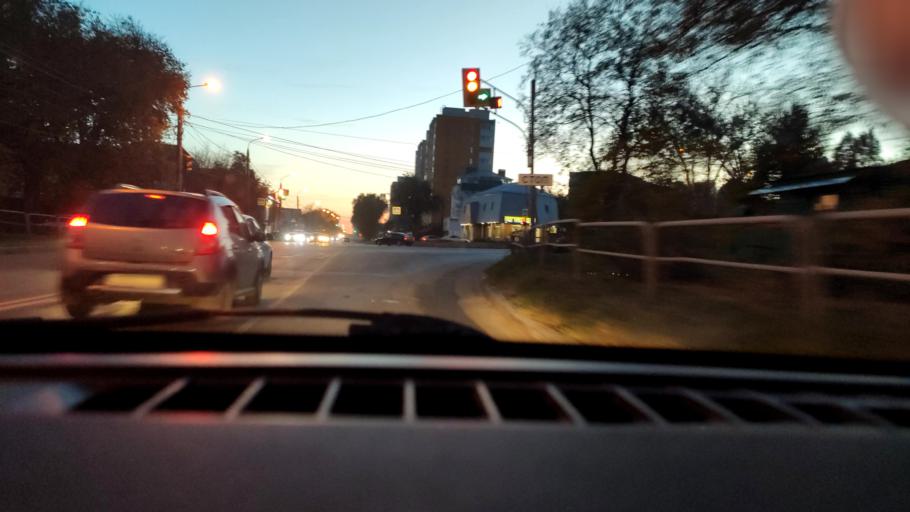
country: RU
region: Samara
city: Samara
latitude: 53.1882
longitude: 50.2072
